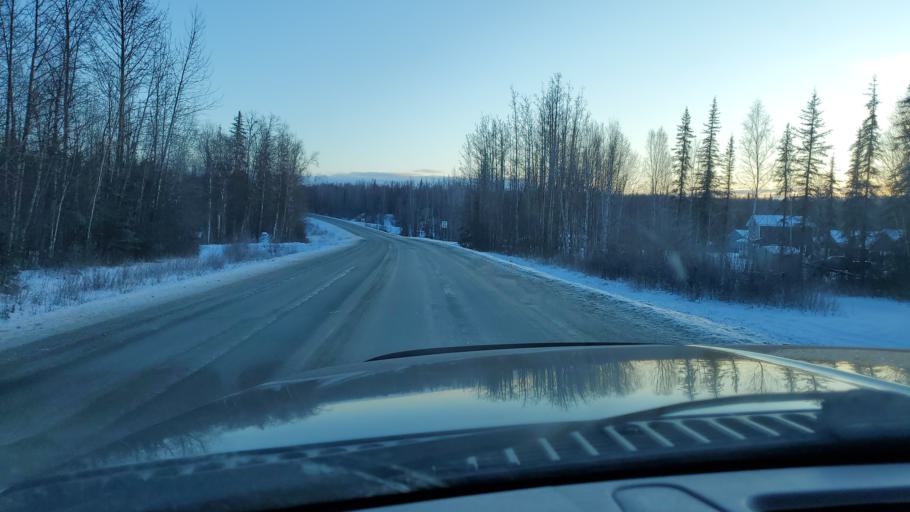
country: US
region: Alaska
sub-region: Matanuska-Susitna Borough
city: Fishhook
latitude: 61.6845
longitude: -149.2397
